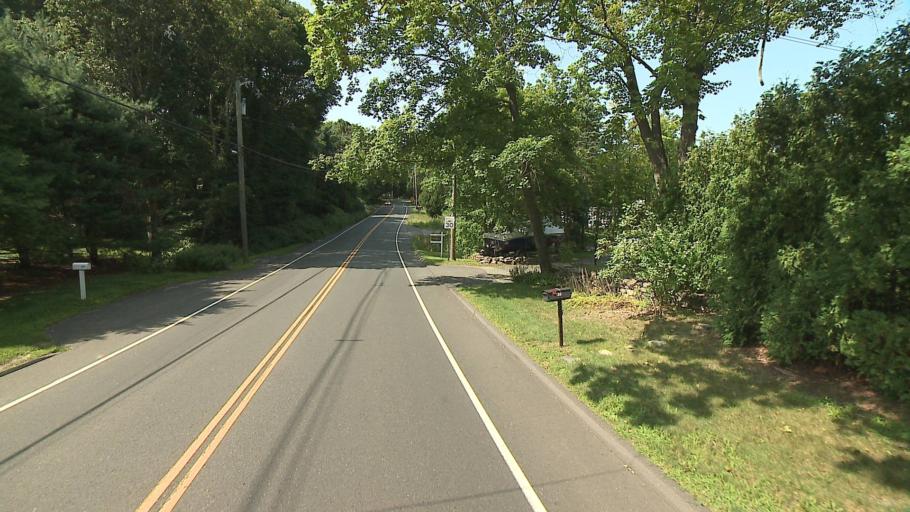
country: US
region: Connecticut
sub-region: Fairfield County
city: Newtown
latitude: 41.4573
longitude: -73.3827
